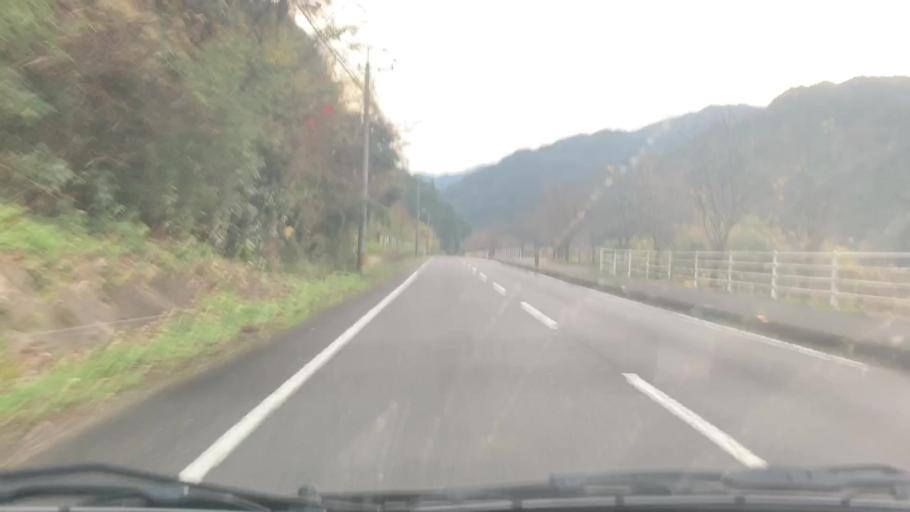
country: JP
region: Saga Prefecture
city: Kashima
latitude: 33.0343
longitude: 130.0699
